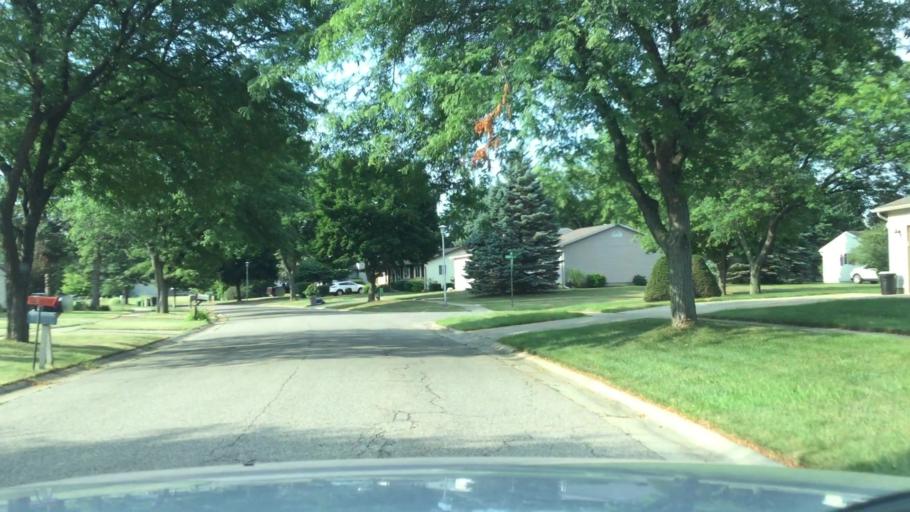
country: US
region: Michigan
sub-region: Genesee County
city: Flushing
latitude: 43.0577
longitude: -83.8654
